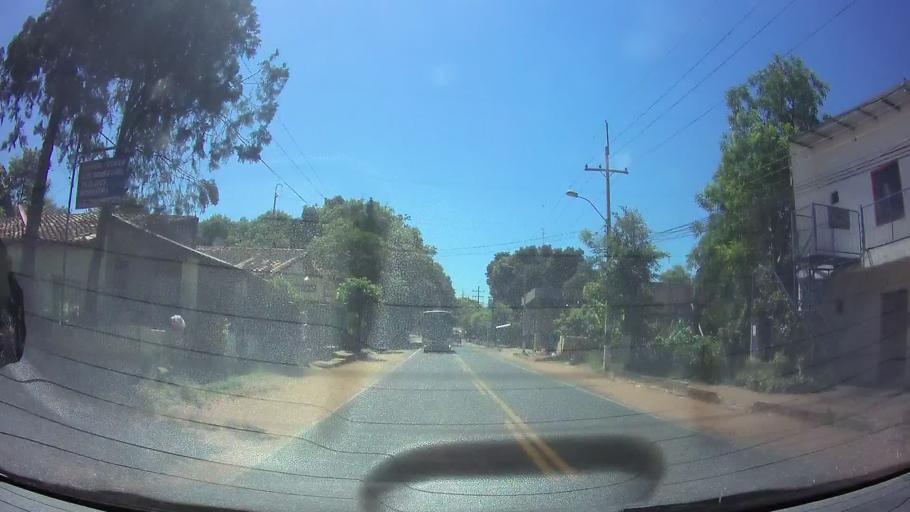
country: PY
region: Central
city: Aregua
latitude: -25.2979
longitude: -57.4141
